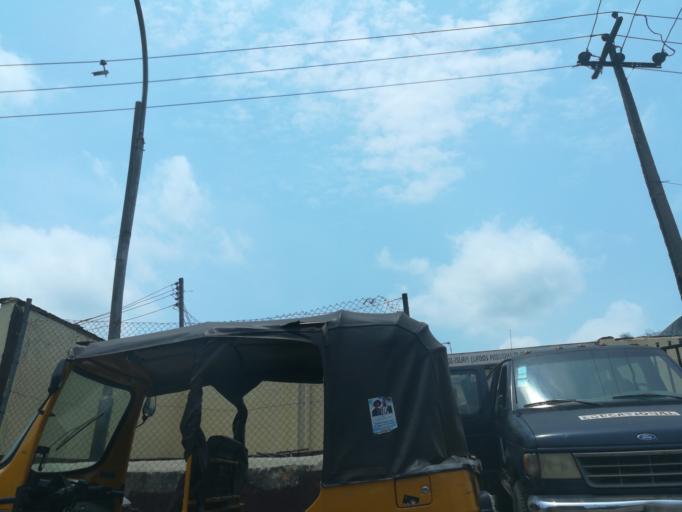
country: NG
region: Lagos
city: Lagos
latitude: 6.4569
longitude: 3.3994
